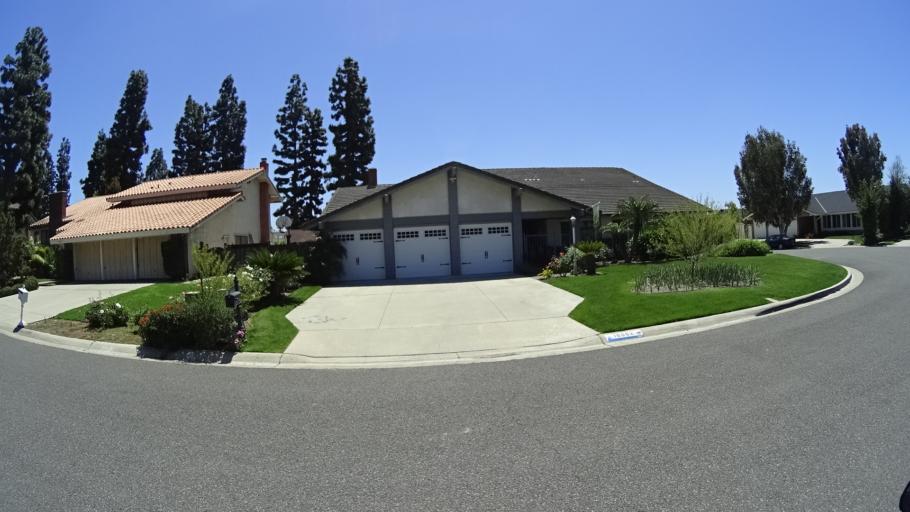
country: US
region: California
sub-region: Orange County
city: Villa Park
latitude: 33.8069
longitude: -117.8173
